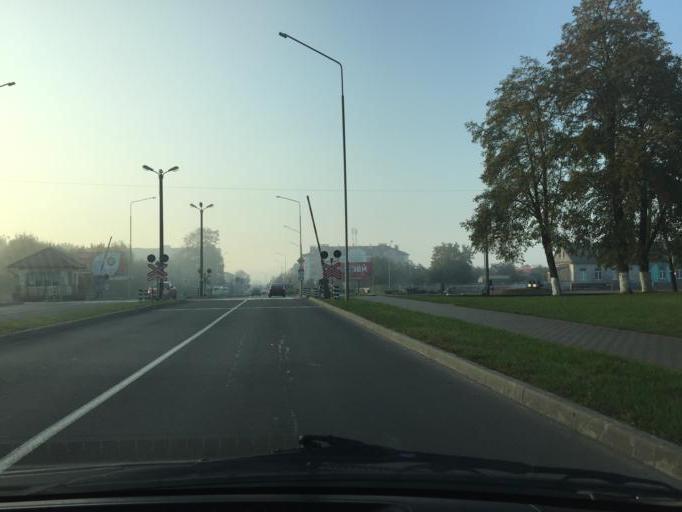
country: BY
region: Brest
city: Pinsk
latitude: 52.1231
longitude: 26.1003
